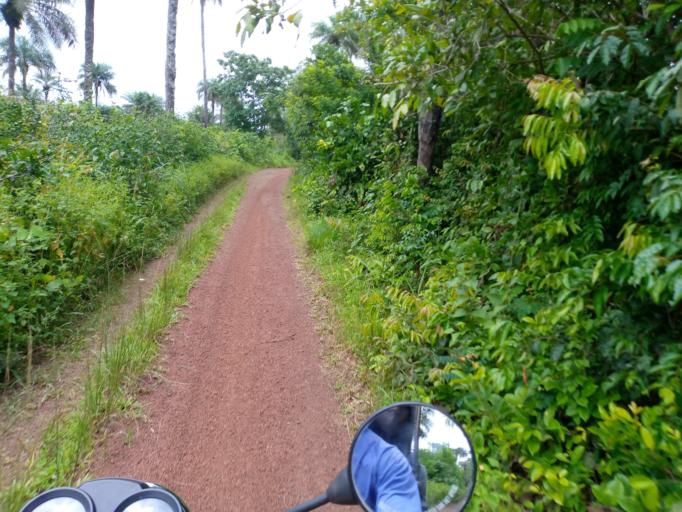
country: SL
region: Northern Province
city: Mange
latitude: 8.9917
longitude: -12.7756
